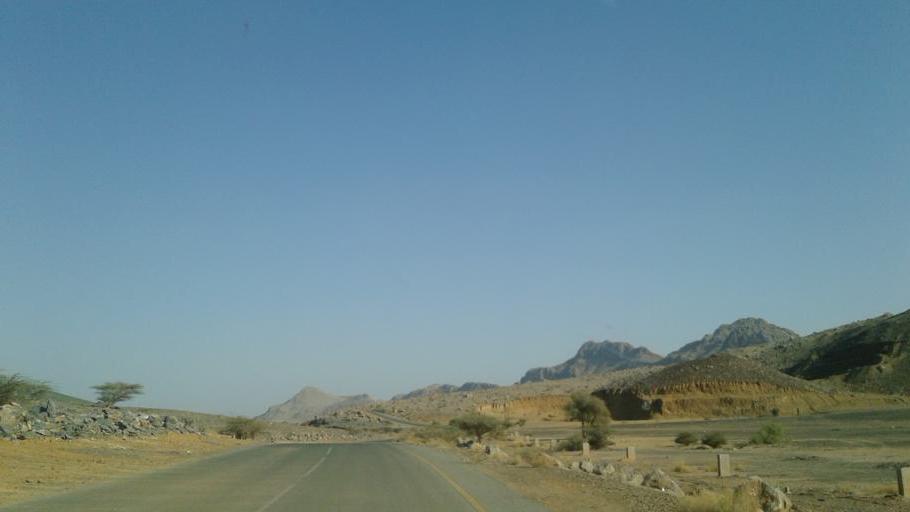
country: OM
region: Muhafazat ad Dakhiliyah
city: Bahla'
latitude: 23.0776
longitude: 57.3546
